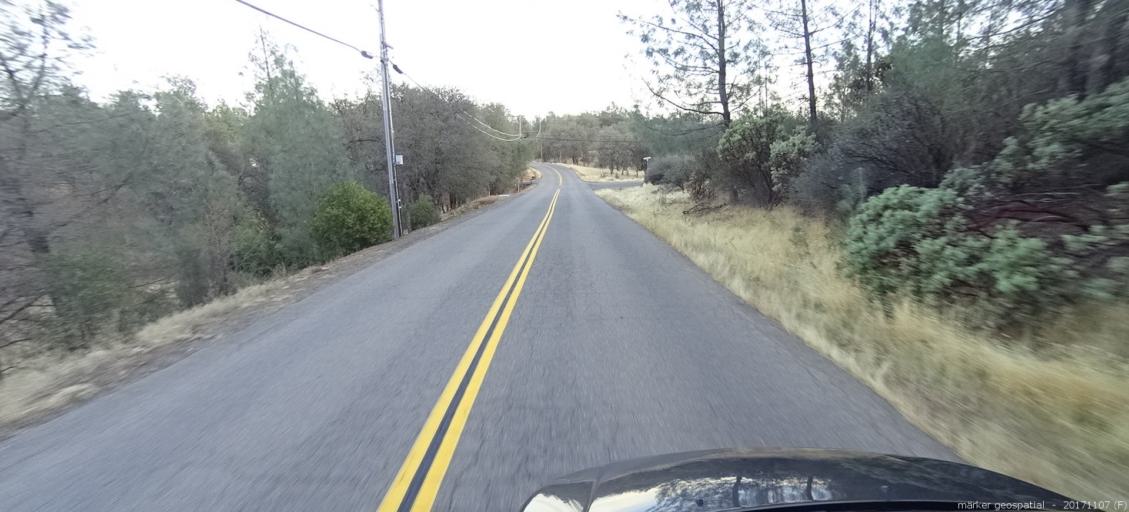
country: US
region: California
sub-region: Shasta County
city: Shasta
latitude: 40.5419
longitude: -122.4832
